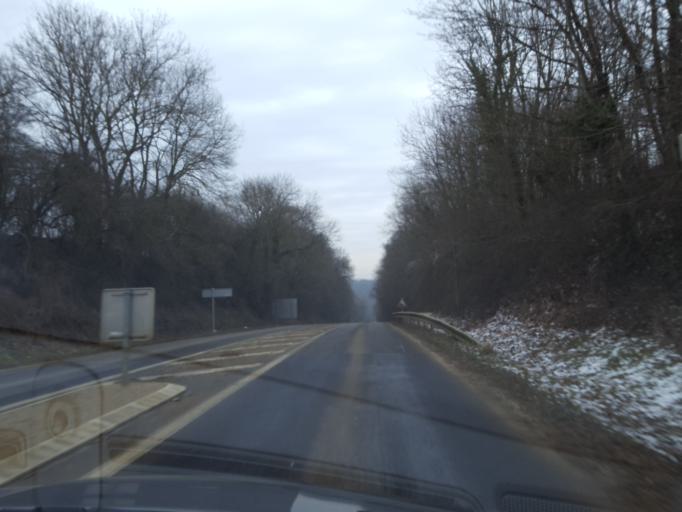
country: FR
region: Lorraine
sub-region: Departement de la Moselle
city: Chatel-Saint-Germain
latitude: 49.1145
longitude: 6.0315
